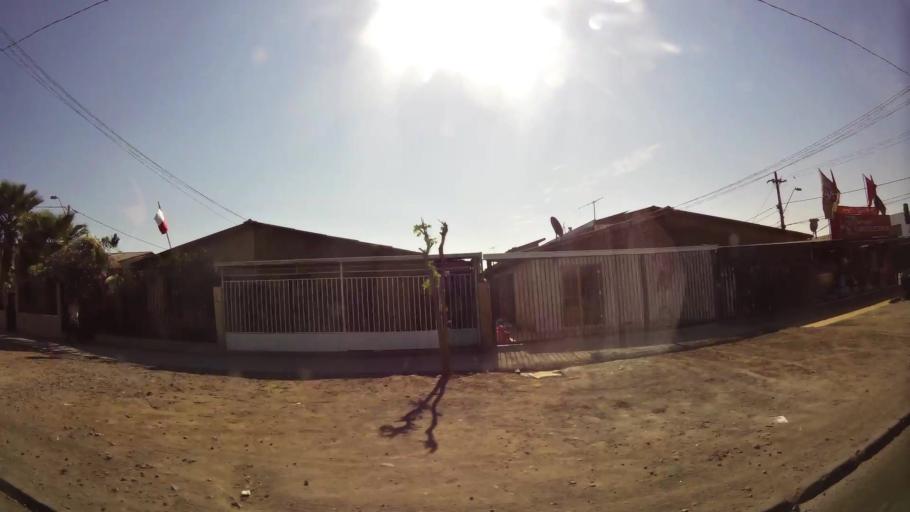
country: CL
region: Santiago Metropolitan
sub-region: Provincia de Santiago
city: Santiago
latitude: -33.5142
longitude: -70.6931
